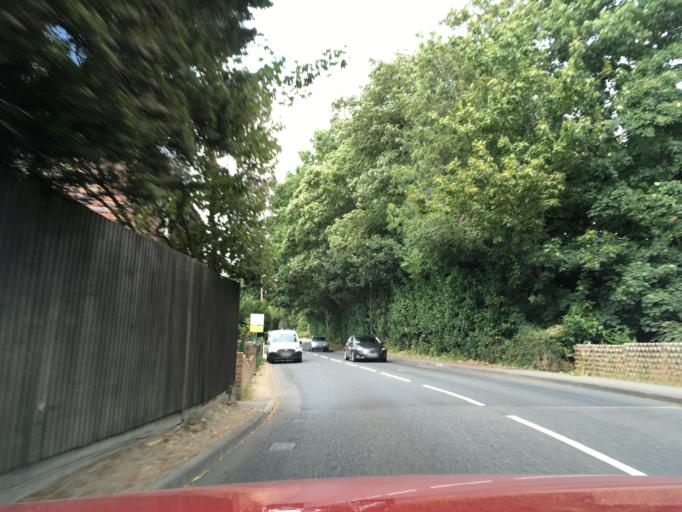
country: GB
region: England
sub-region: Kent
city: Tenterden
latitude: 51.0776
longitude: 0.6951
